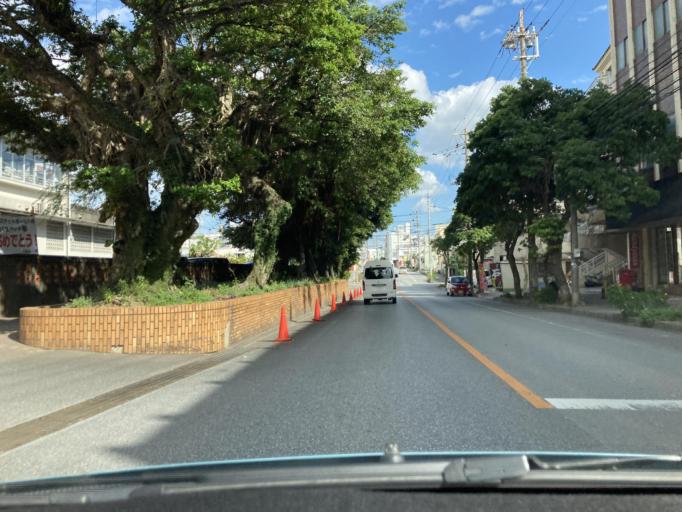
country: JP
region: Okinawa
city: Chatan
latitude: 26.3197
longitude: 127.7804
